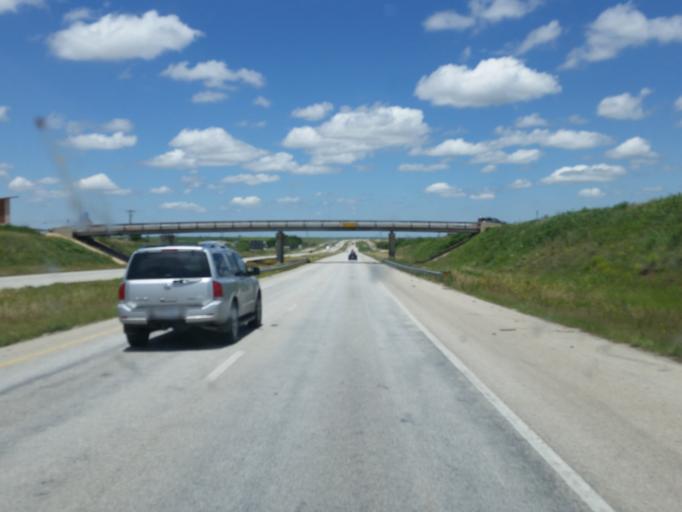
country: US
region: Texas
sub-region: Nolan County
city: Sweetwater
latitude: 32.4540
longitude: -100.3901
